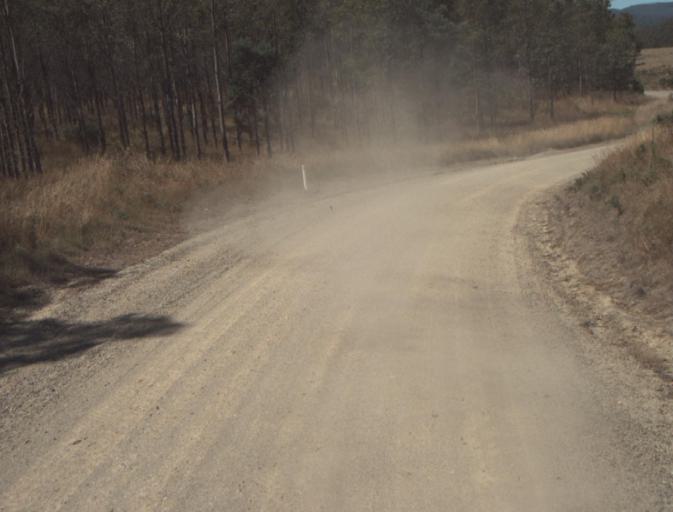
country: AU
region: Tasmania
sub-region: Dorset
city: Scottsdale
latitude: -41.3298
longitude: 147.4392
